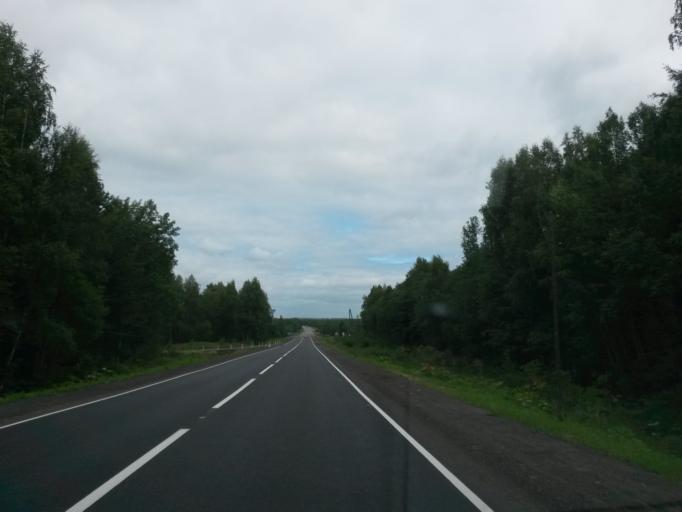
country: RU
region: Jaroslavl
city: Yaroslavl
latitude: 57.5038
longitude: 39.8988
